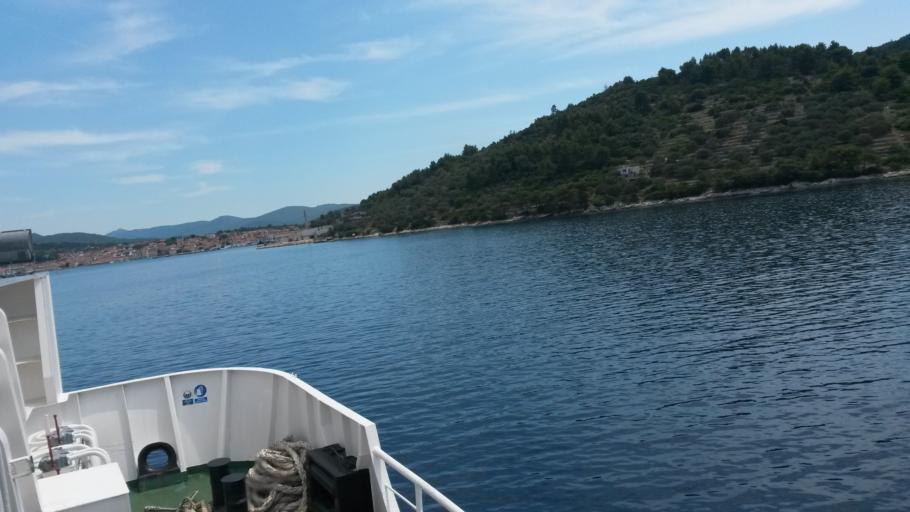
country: HR
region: Dubrovacko-Neretvanska
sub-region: Grad Dubrovnik
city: Vela Luka
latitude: 42.9622
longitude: 16.6961
